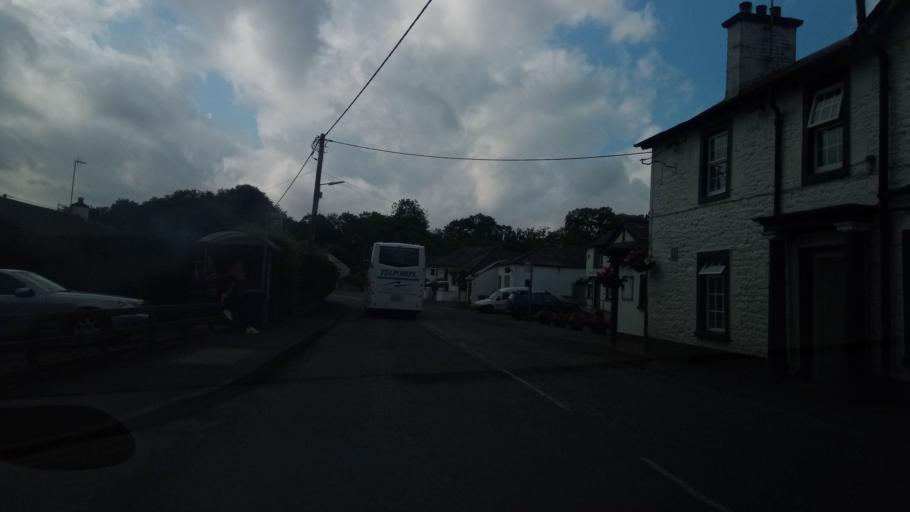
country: GB
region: Scotland
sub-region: Dumfries and Galloway
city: Langholm
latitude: 55.0765
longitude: -2.9537
